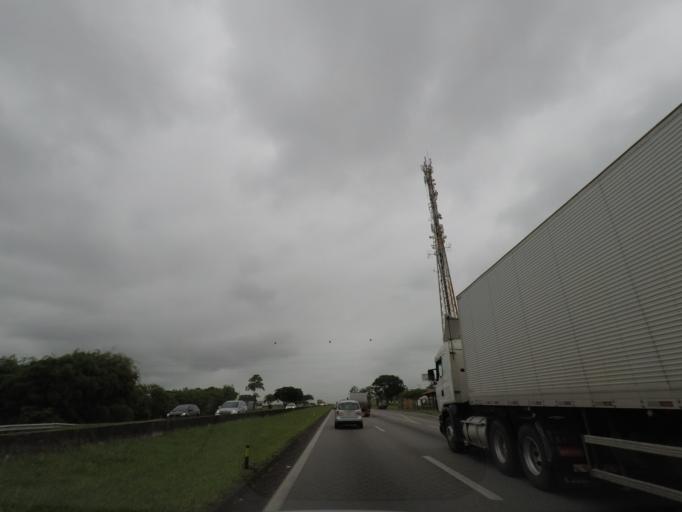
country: BR
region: Sao Paulo
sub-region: Cacapava
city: Cacapava
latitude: -23.1536
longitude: -45.7885
